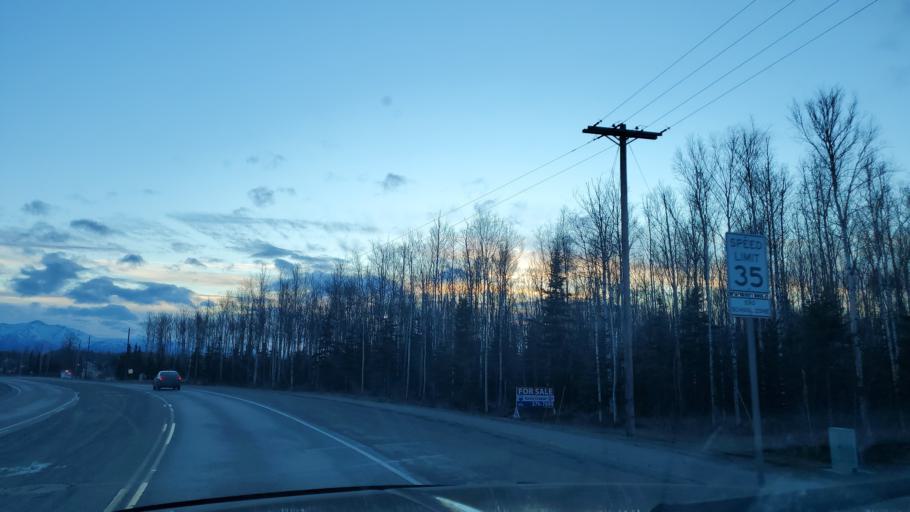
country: US
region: Alaska
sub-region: Matanuska-Susitna Borough
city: Wasilla
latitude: 61.5887
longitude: -149.4435
